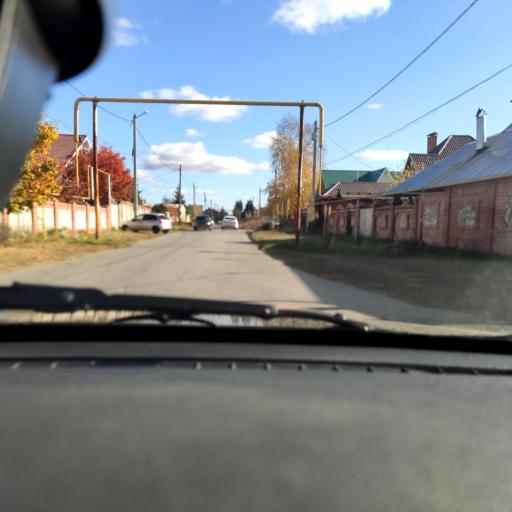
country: RU
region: Samara
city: Podstepki
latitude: 53.5137
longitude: 49.2343
